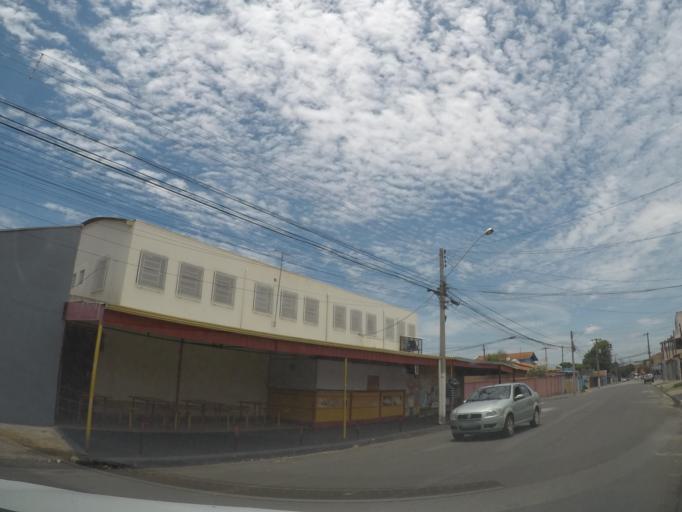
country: BR
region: Sao Paulo
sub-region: Hortolandia
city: Hortolandia
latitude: -22.8368
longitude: -47.1925
